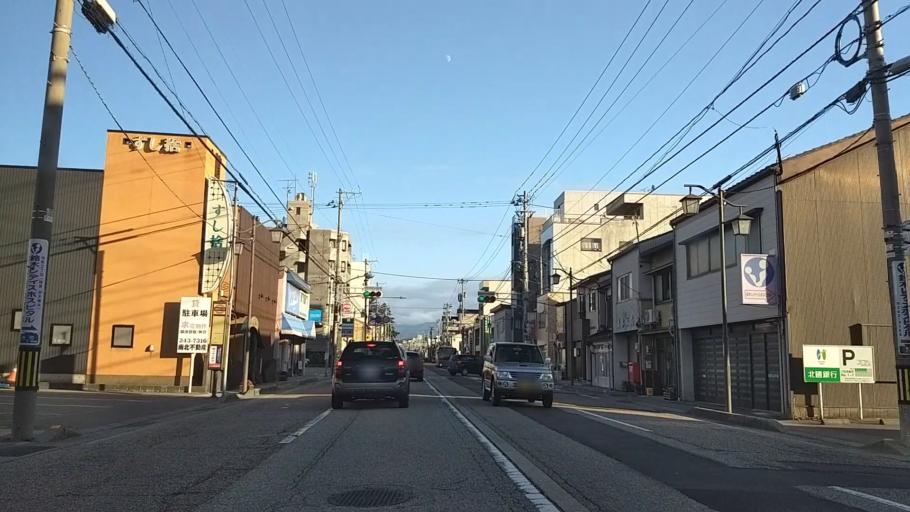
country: JP
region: Ishikawa
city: Nonoichi
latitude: 36.5493
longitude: 136.6566
